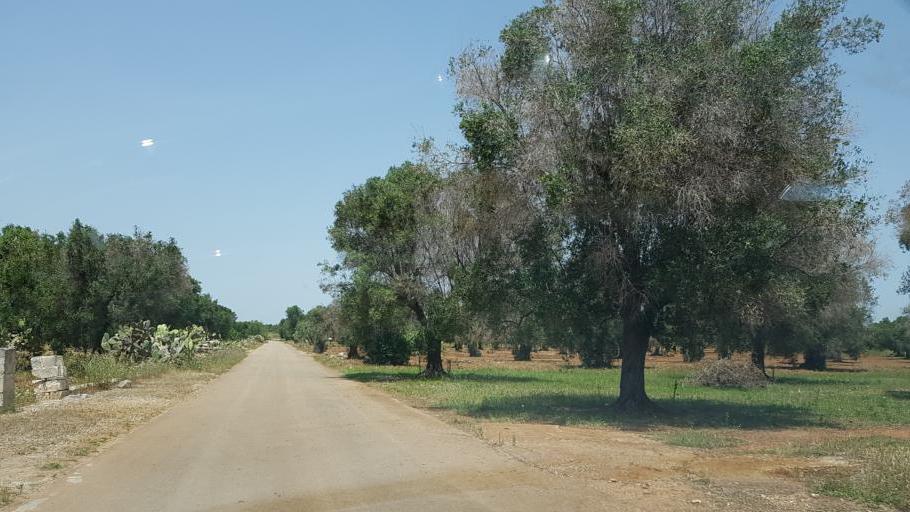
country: IT
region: Apulia
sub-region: Provincia di Lecce
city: Porto Cesareo
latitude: 40.3214
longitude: 17.8935
